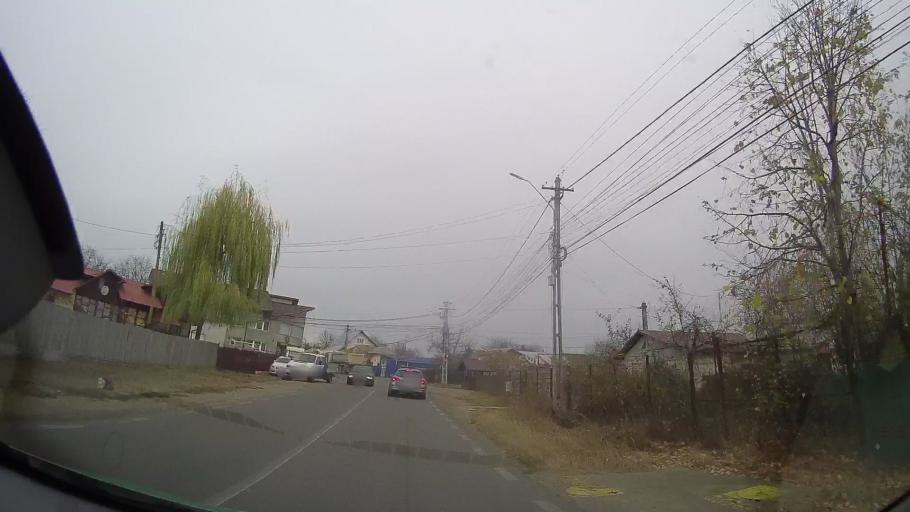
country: RO
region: Prahova
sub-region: Oras Baicoi
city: Liliesti
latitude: 45.0306
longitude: 25.8871
